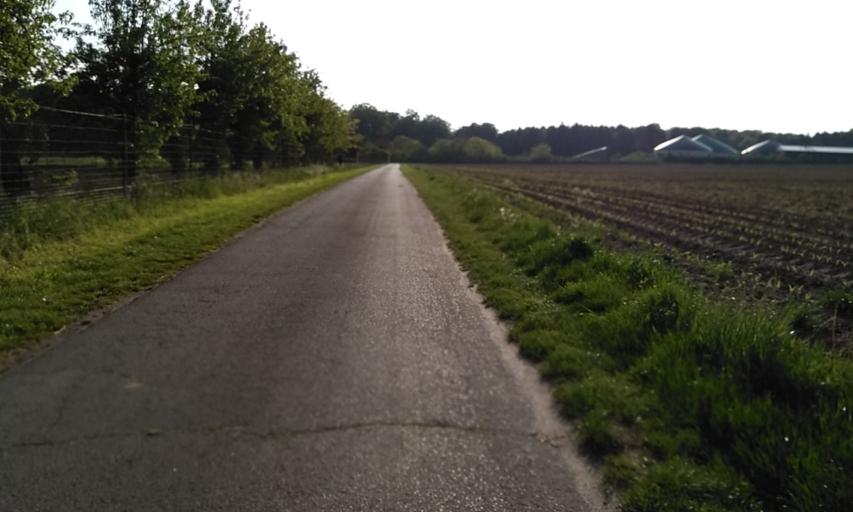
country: DE
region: Lower Saxony
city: Horneburg
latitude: 53.4992
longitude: 9.5617
